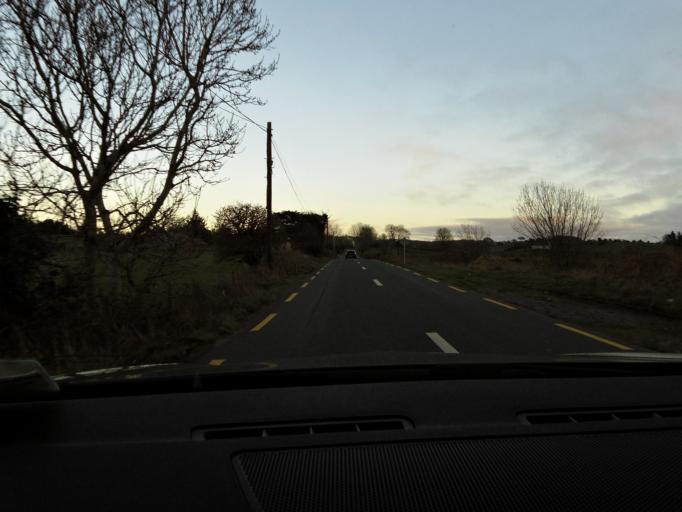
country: IE
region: Connaught
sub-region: Sligo
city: Ballymote
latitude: 53.9775
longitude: -8.4551
